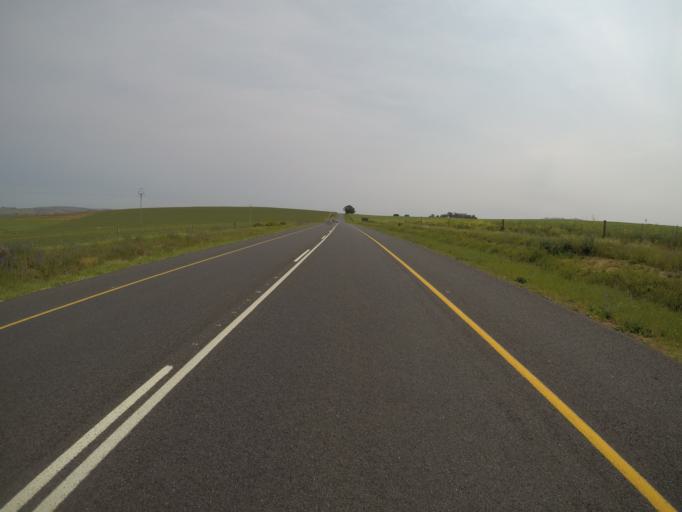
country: ZA
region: Western Cape
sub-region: West Coast District Municipality
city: Malmesbury
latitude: -33.5091
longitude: 18.8430
